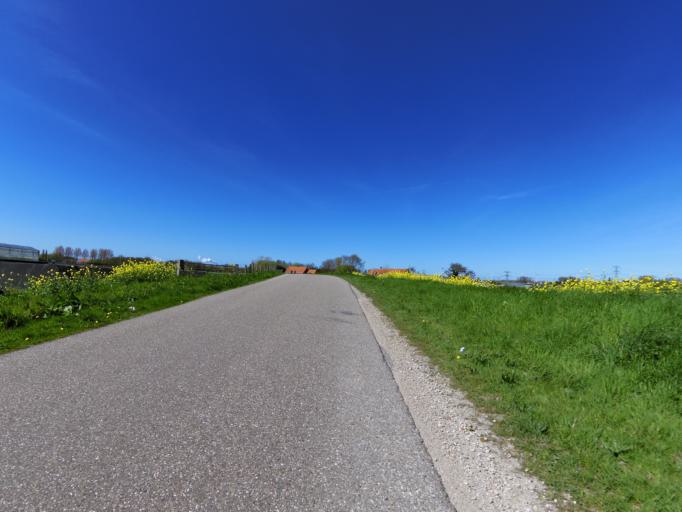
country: NL
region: South Holland
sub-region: Gemeente Brielle
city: Brielle
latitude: 51.9017
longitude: 4.1212
